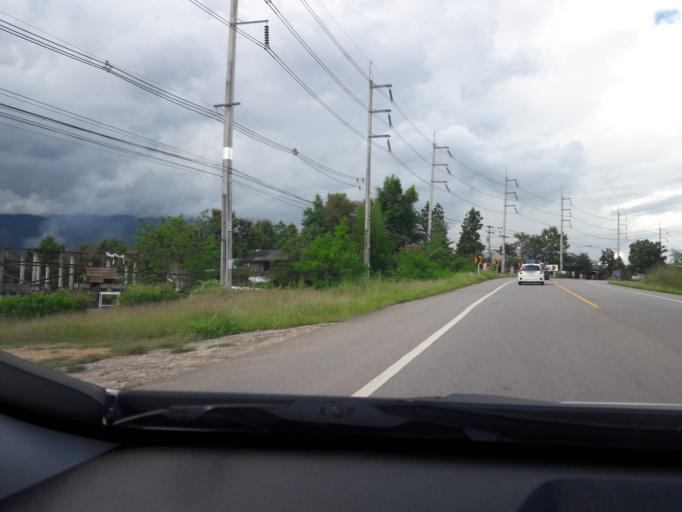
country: TH
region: Mae Hong Son
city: Mae Hi
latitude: 19.3337
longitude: 98.4322
